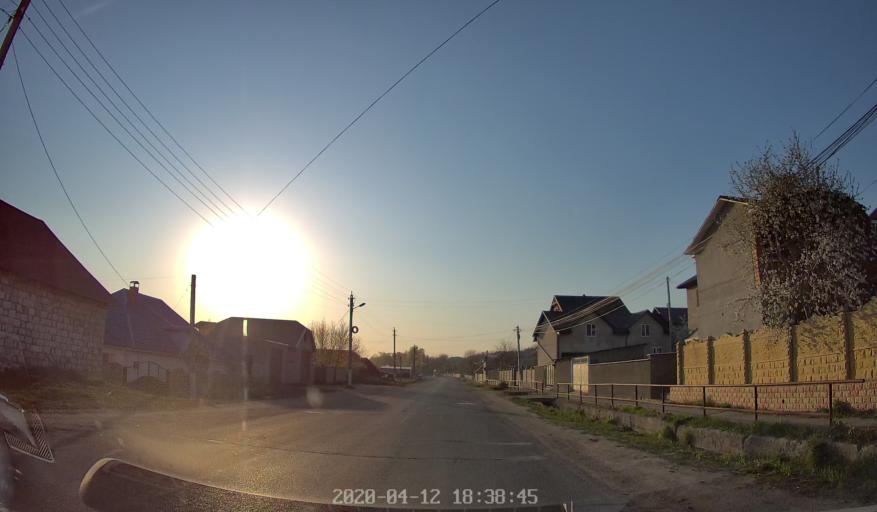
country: MD
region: Chisinau
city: Vadul lui Voda
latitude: 47.1256
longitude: 28.9967
